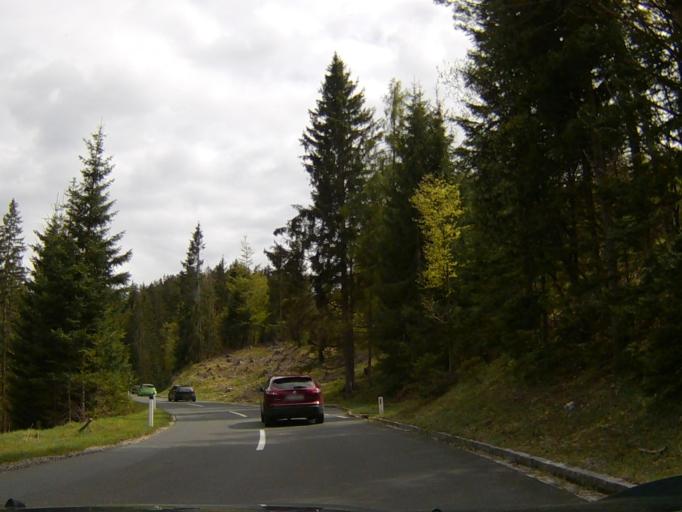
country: AT
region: Carinthia
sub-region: Politischer Bezirk Villach Land
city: Arnoldstein
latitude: 46.5943
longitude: 13.7689
